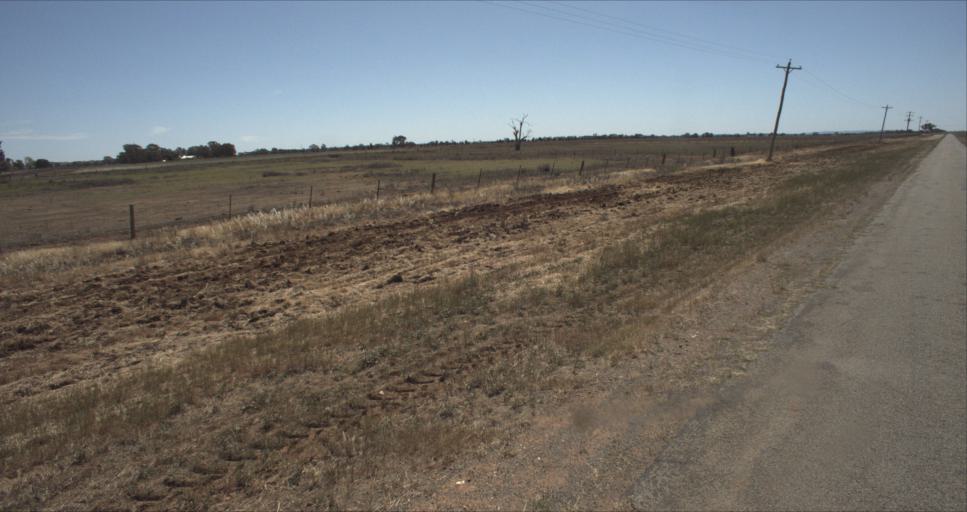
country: AU
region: New South Wales
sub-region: Leeton
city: Leeton
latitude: -34.5099
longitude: 146.3448
